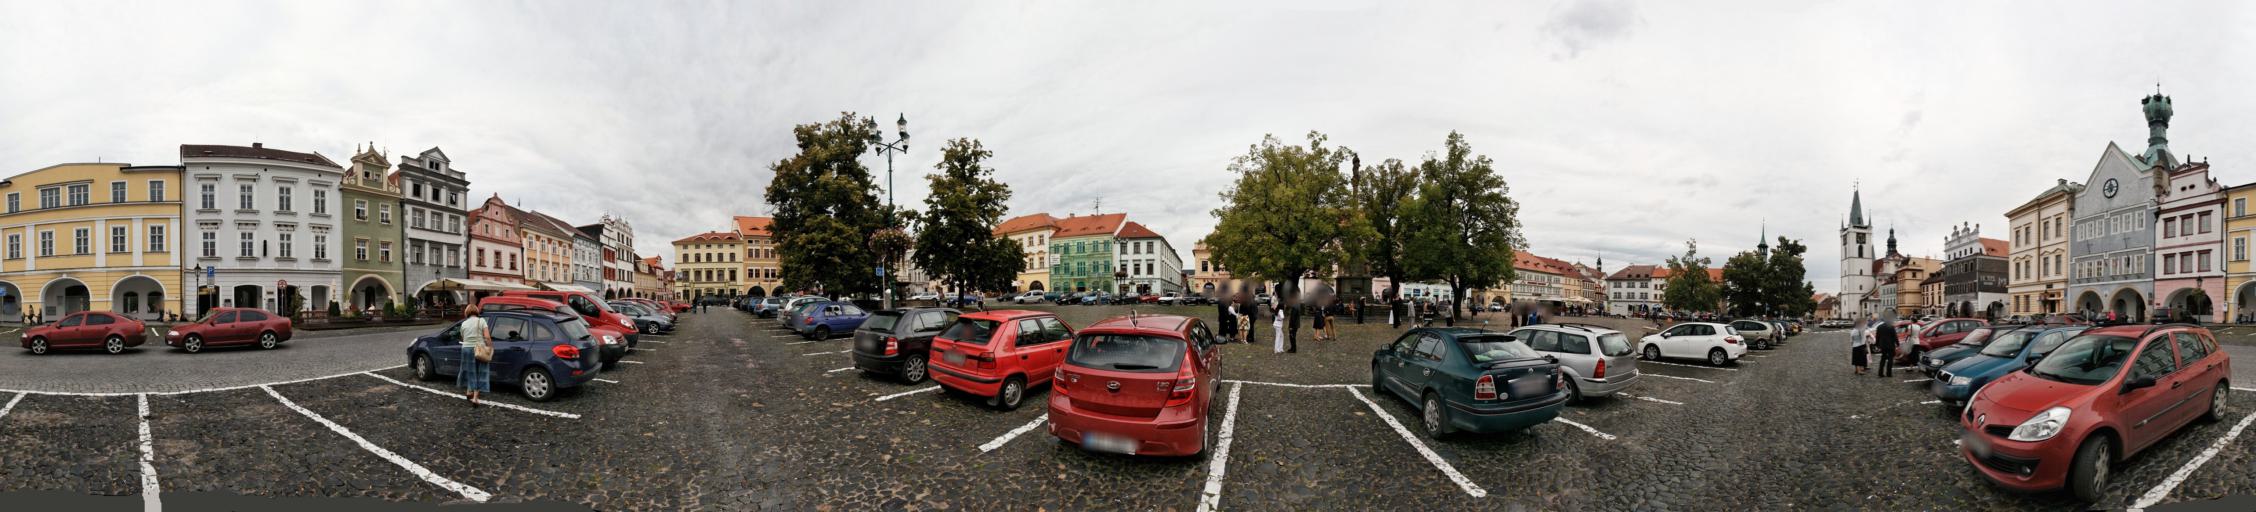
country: CZ
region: Ustecky
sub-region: Okres Litomerice
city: Litomerice
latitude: 50.5336
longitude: 14.1309
